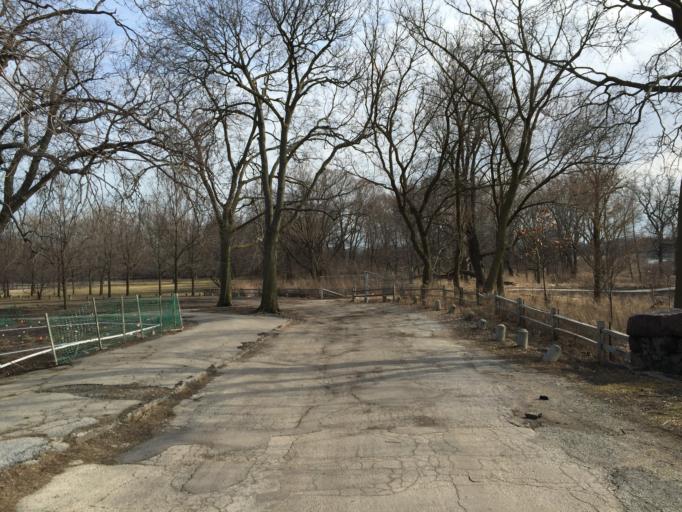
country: US
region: Illinois
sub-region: Cook County
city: Chicago
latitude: 41.7871
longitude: -87.5806
